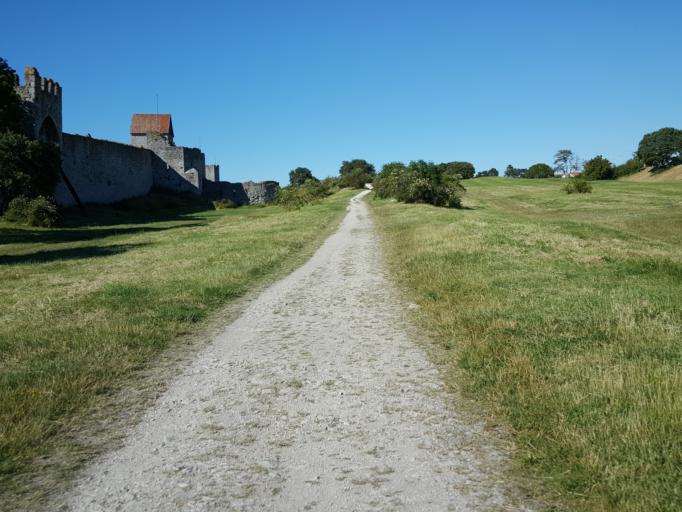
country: SE
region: Gotland
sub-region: Gotland
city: Visby
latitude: 57.6399
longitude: 18.3003
